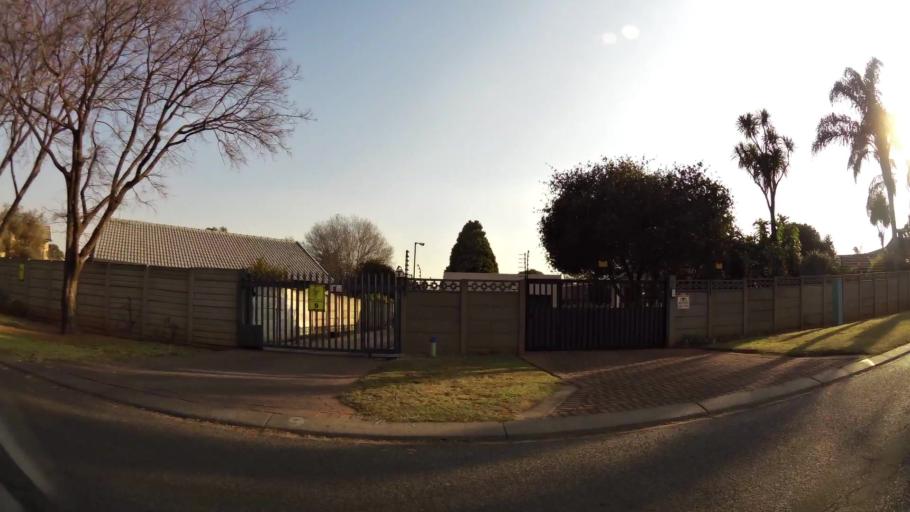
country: ZA
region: Gauteng
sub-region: City of Johannesburg Metropolitan Municipality
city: Modderfontein
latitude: -26.0672
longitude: 28.2209
